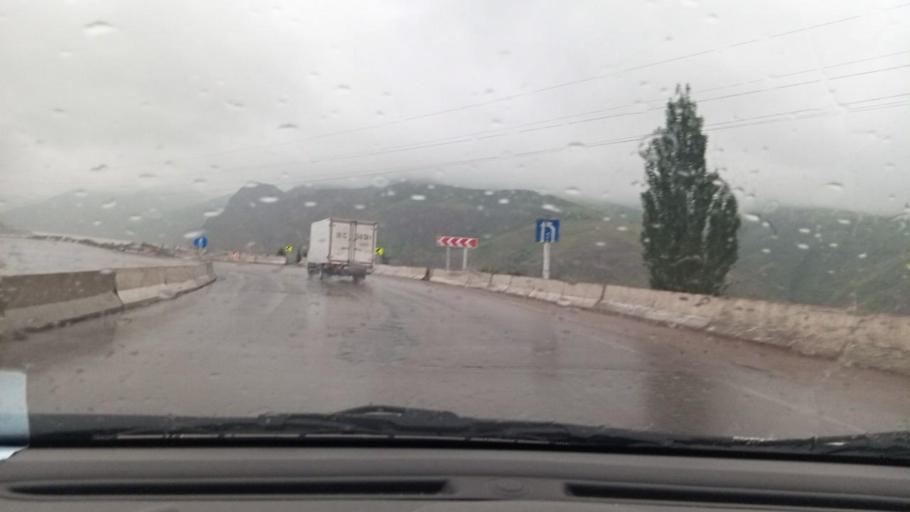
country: UZ
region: Toshkent
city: Angren
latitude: 41.0692
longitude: 70.2388
